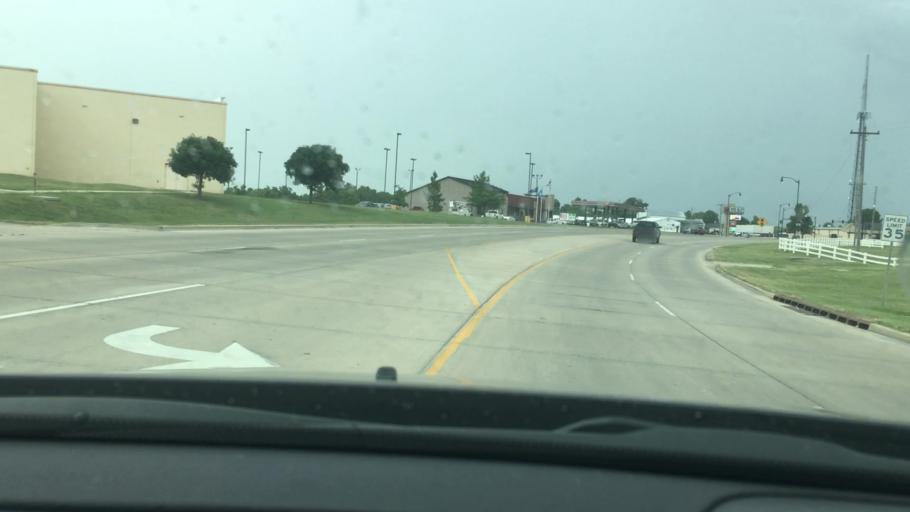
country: US
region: Oklahoma
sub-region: Pontotoc County
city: Ada
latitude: 34.7716
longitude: -96.6985
